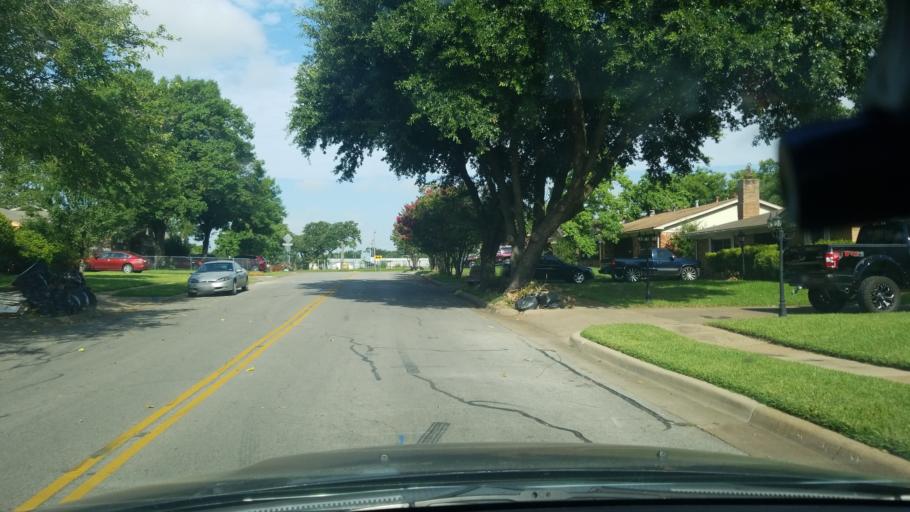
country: US
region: Texas
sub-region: Dallas County
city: Balch Springs
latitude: 32.7433
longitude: -96.6723
